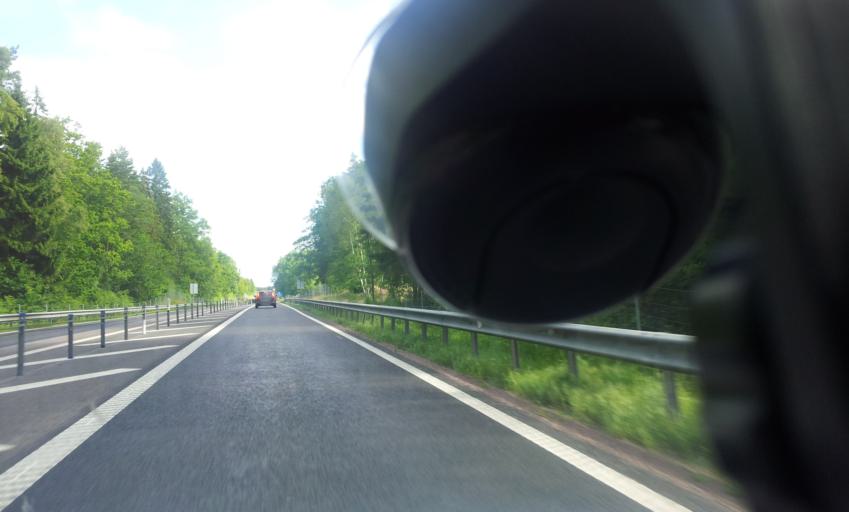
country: SE
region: Kalmar
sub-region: Monsteras Kommun
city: Timmernabben
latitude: 56.9052
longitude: 16.3797
